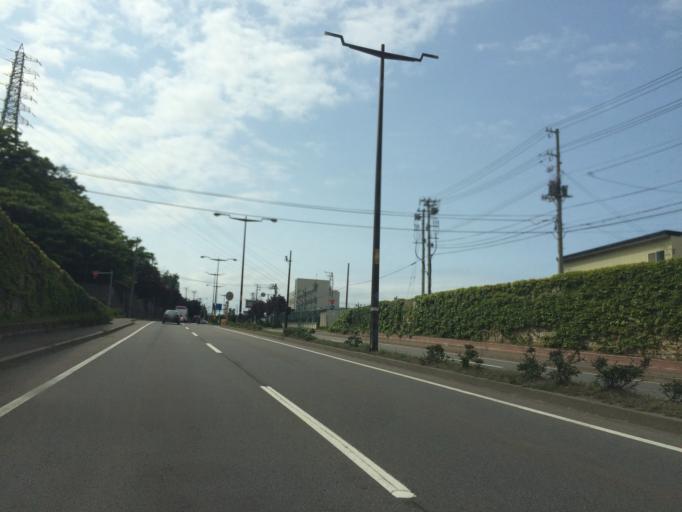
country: JP
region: Hokkaido
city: Otaru
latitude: 43.2058
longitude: 140.9820
